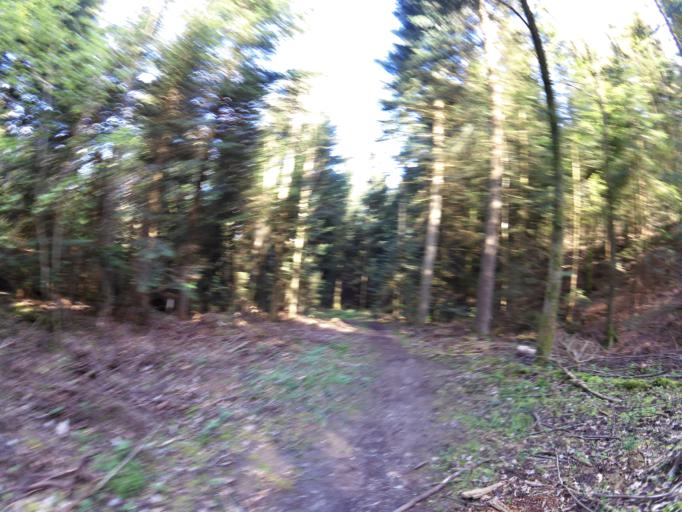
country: CH
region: Aargau
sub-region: Bezirk Aarau
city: Aarau
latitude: 47.4015
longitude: 8.0342
